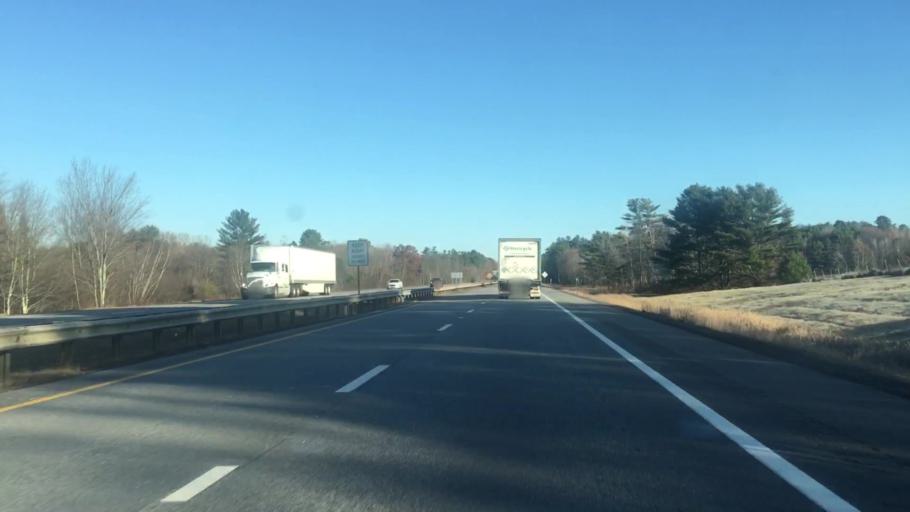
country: US
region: Maine
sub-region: Cumberland County
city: New Gloucester
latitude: 43.9120
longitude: -70.3392
